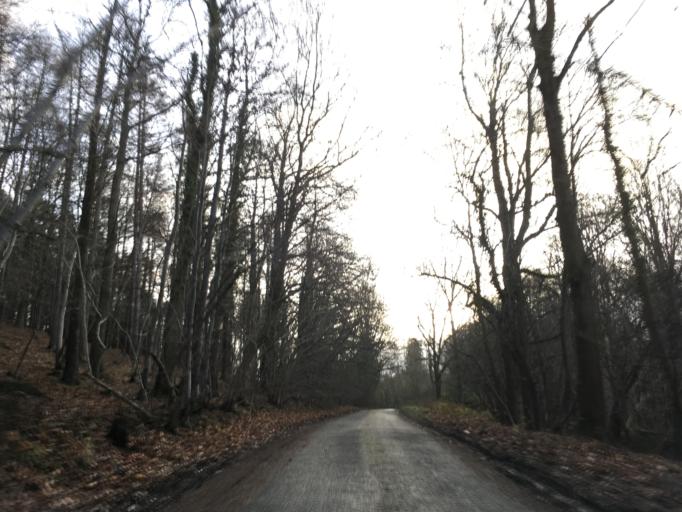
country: GB
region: England
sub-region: South Gloucestershire
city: Falfield
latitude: 51.6481
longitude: -2.4311
